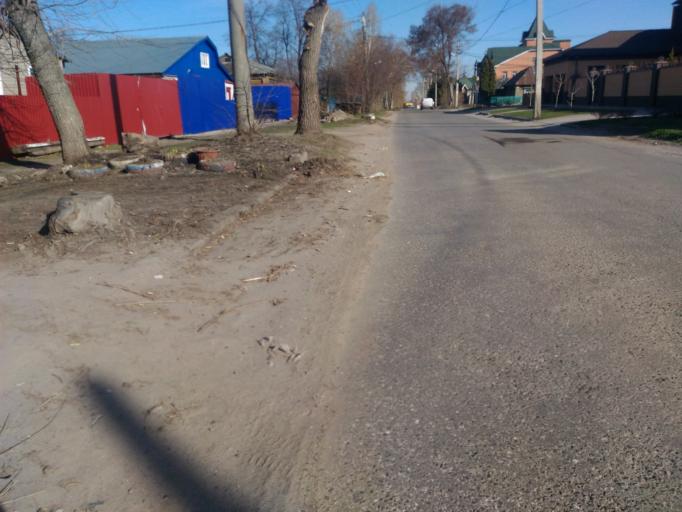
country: RU
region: Ulyanovsk
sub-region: Ulyanovskiy Rayon
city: Ulyanovsk
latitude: 54.3473
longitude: 48.3801
